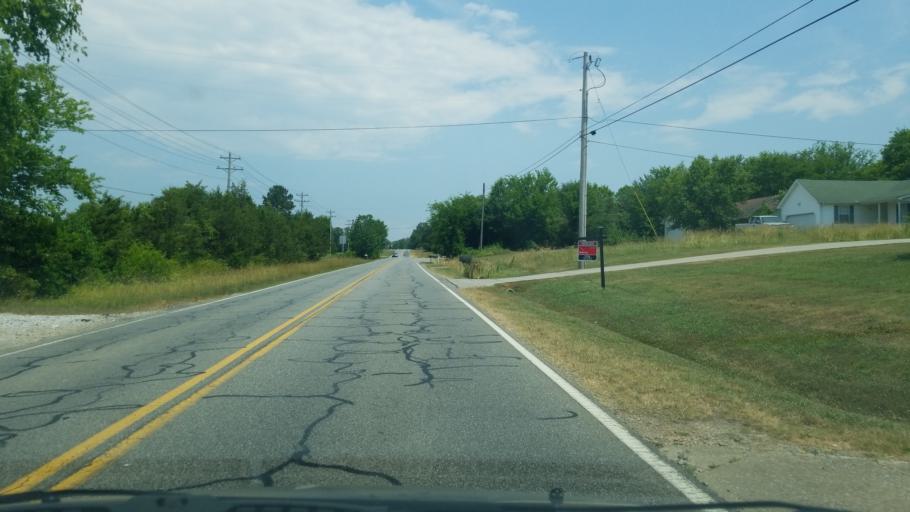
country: US
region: Tennessee
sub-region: Hamilton County
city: East Brainerd
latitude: 34.9806
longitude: -85.0973
